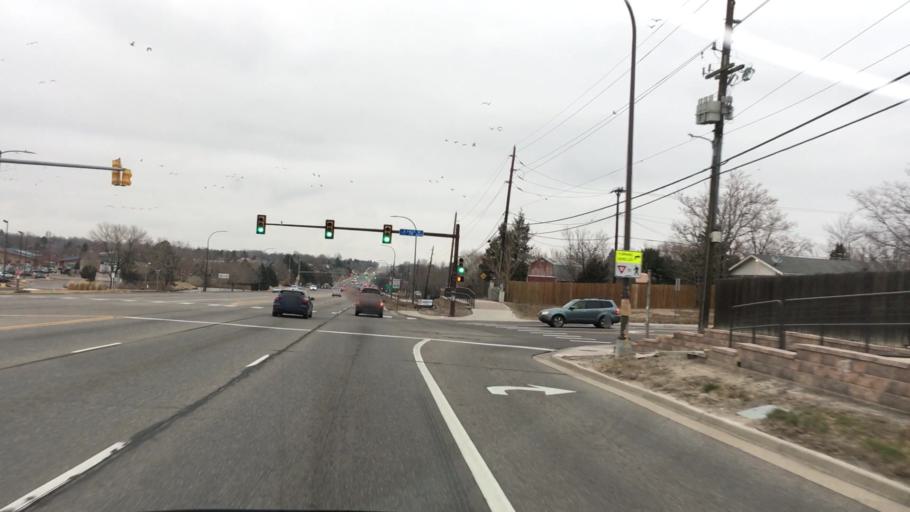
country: US
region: Colorado
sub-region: Jefferson County
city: Arvada
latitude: 39.8346
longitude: -105.0816
